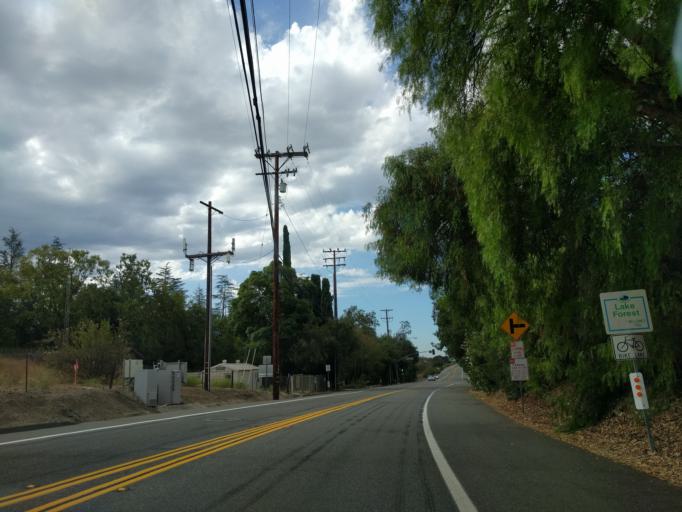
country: US
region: California
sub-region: Orange County
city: Portola Hills
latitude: 33.6830
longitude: -117.6208
